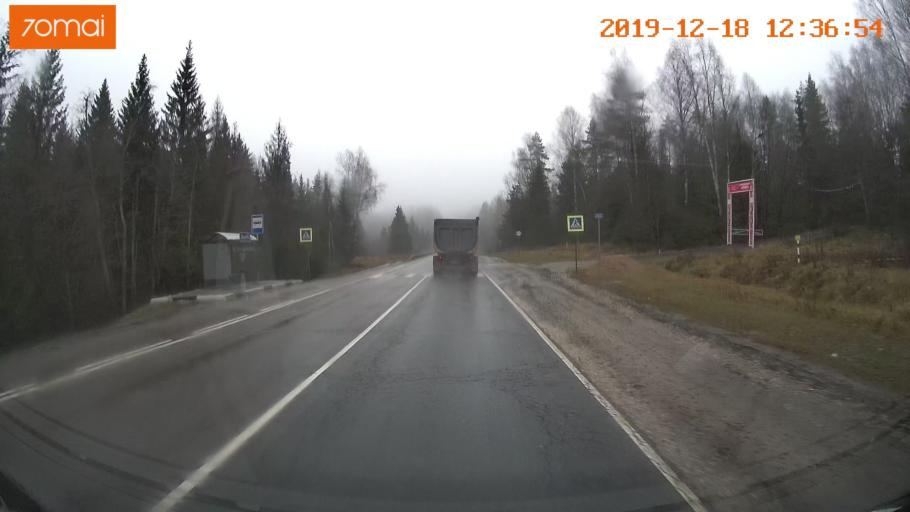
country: RU
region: Moskovskaya
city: Rumyantsevo
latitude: 56.1404
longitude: 36.5976
